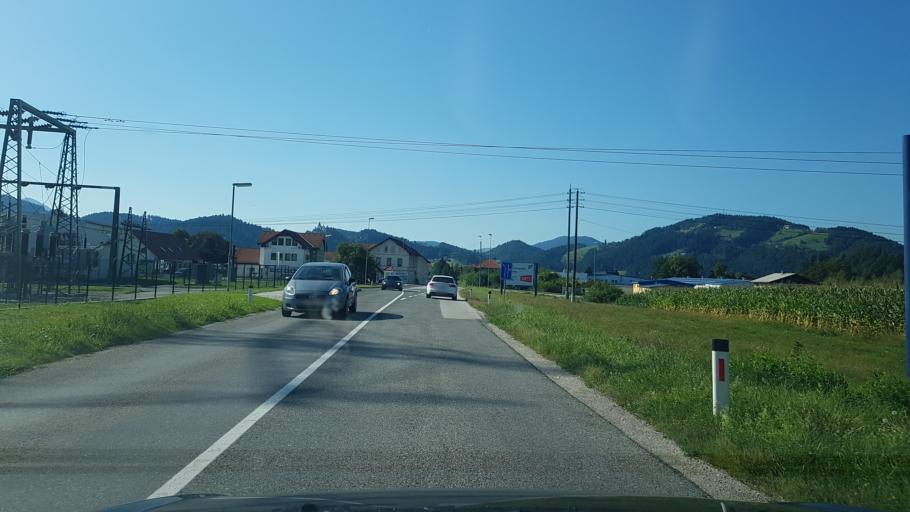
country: SI
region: Slovenj Gradec
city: Slovenj Gradec
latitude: 46.4999
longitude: 15.0930
